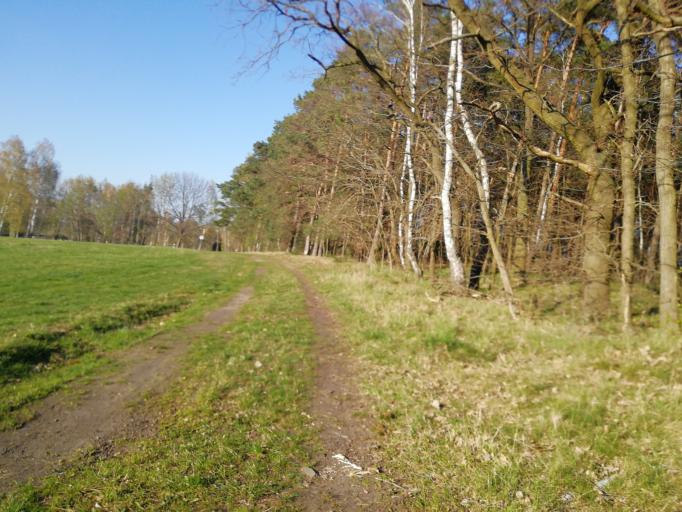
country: DE
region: Brandenburg
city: Calau
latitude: 51.7244
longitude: 13.9653
